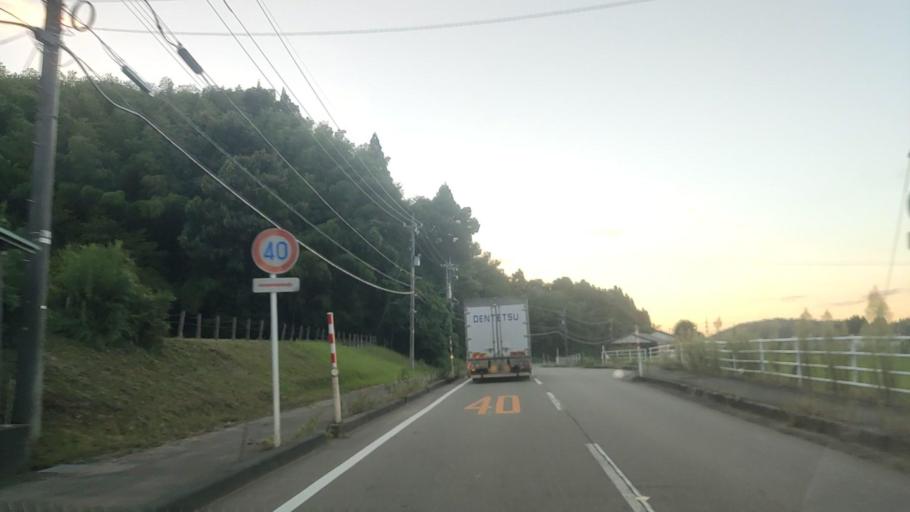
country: JP
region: Ishikawa
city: Tsubata
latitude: 36.6568
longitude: 136.7560
